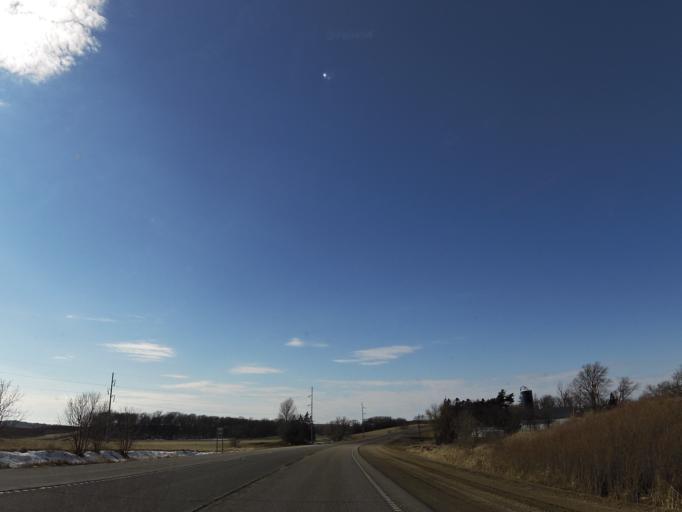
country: US
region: Minnesota
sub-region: Le Sueur County
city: Waterville
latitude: 44.1969
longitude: -93.5274
